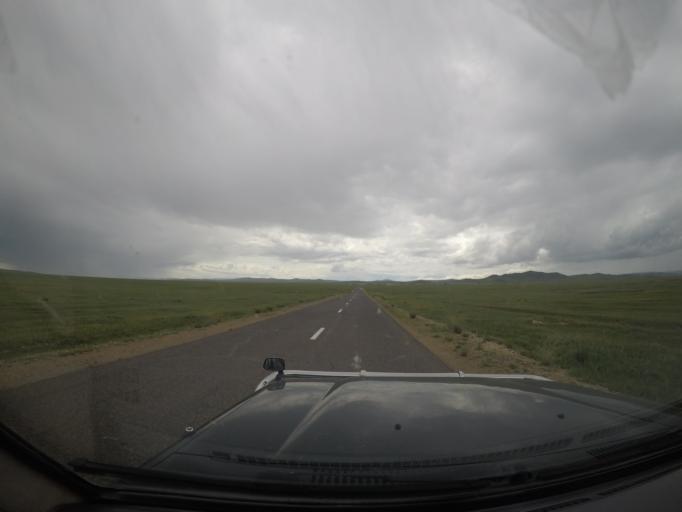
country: MN
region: Hentiy
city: Avraga
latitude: 47.4821
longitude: 109.4994
